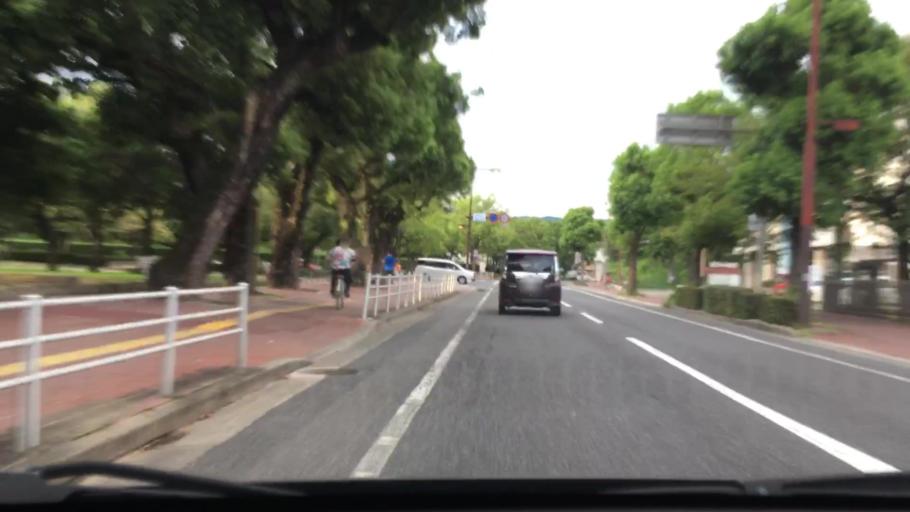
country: JP
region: Hyogo
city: Himeji
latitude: 34.8408
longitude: 134.6981
